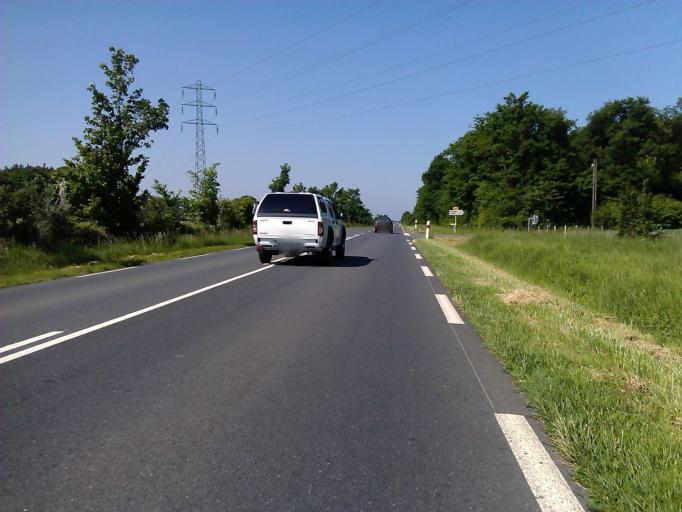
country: FR
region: Centre
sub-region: Departement de l'Indre
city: Arthon
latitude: 46.6134
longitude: 1.6751
